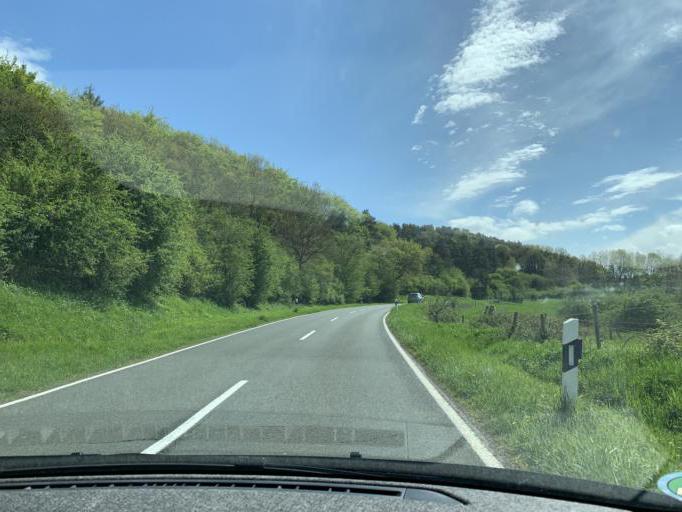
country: DE
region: North Rhine-Westphalia
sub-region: Regierungsbezirk Koln
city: Mechernich
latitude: 50.5731
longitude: 6.6991
